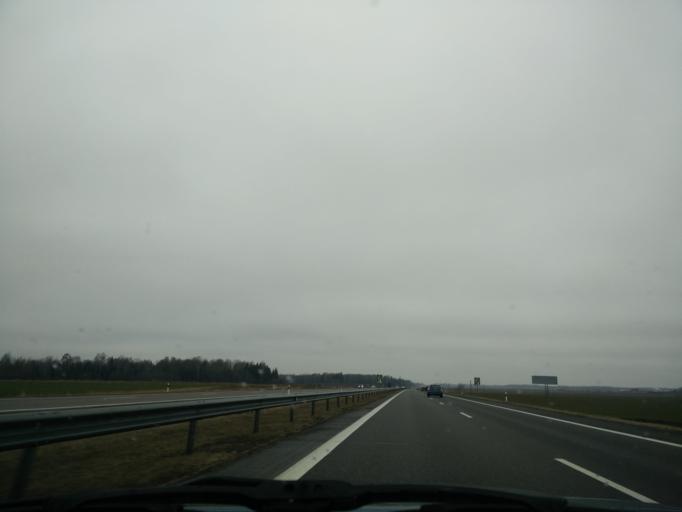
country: LT
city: Raseiniai
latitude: 55.3713
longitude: 22.9613
